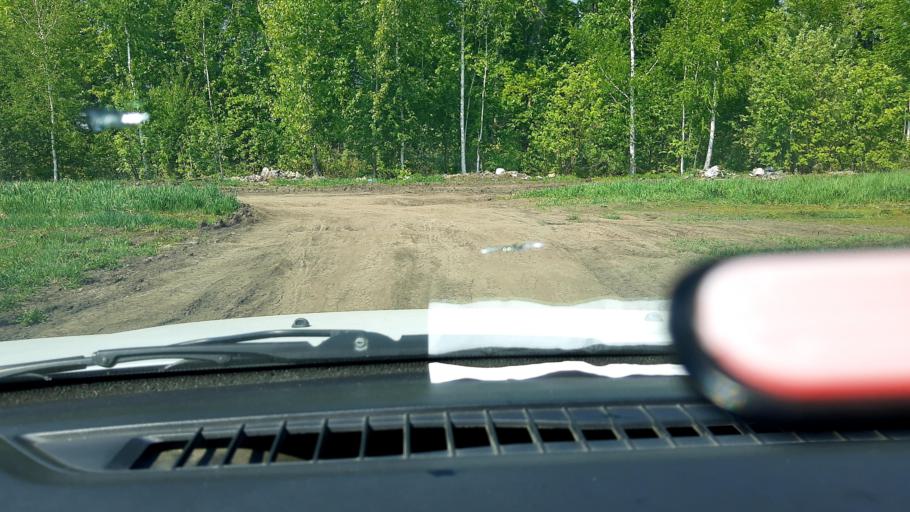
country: RU
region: Bashkortostan
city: Kabakovo
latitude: 54.6988
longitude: 56.1731
